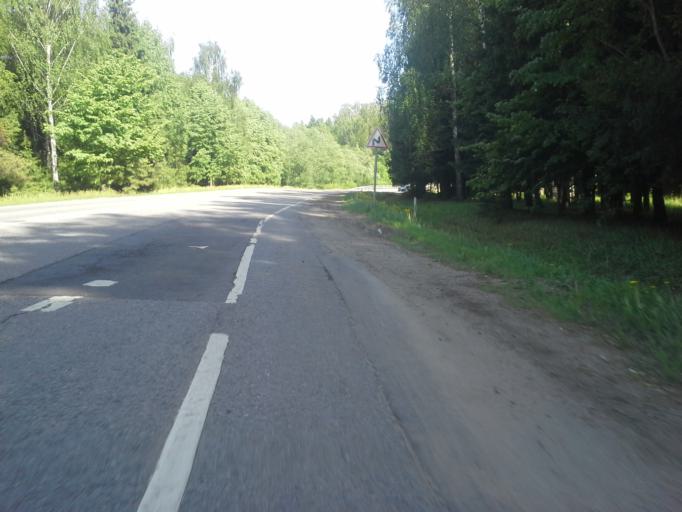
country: RU
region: Moskovskaya
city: Troitsk
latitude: 55.4325
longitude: 37.3396
